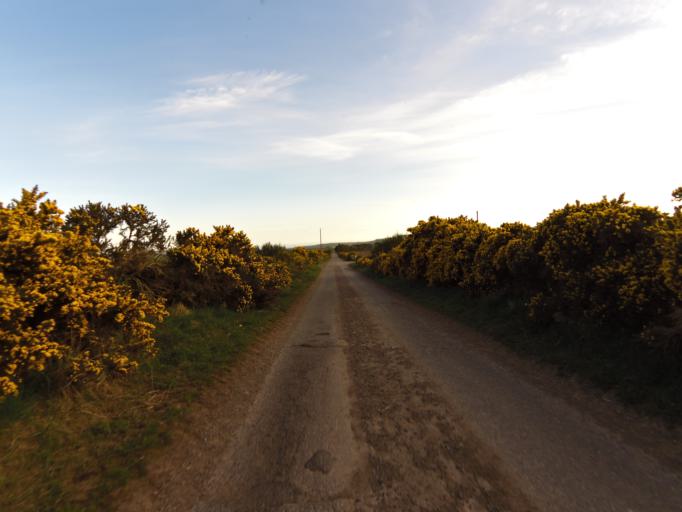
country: GB
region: Scotland
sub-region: Aberdeenshire
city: Stonehaven
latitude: 56.9176
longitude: -2.2273
